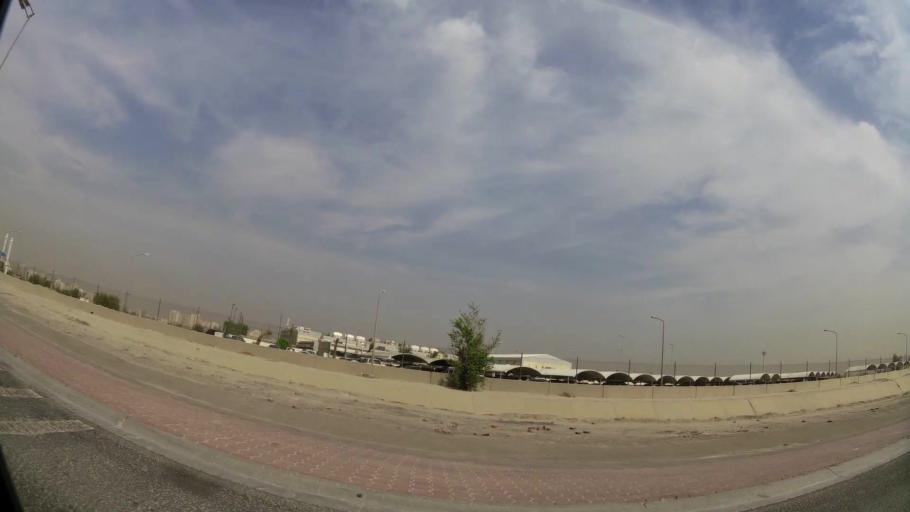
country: KW
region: Al Farwaniyah
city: Janub as Surrah
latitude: 29.2663
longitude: 47.9772
